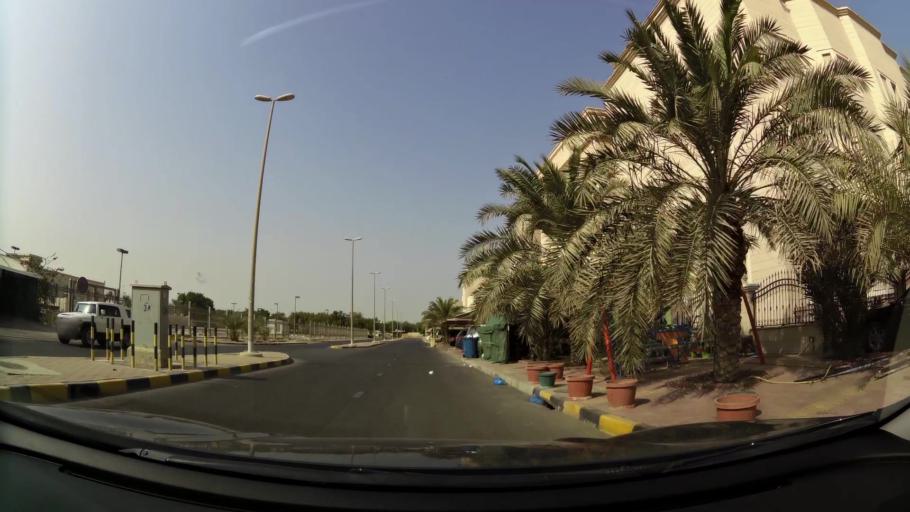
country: KW
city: Bayan
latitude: 29.2878
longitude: 48.0477
